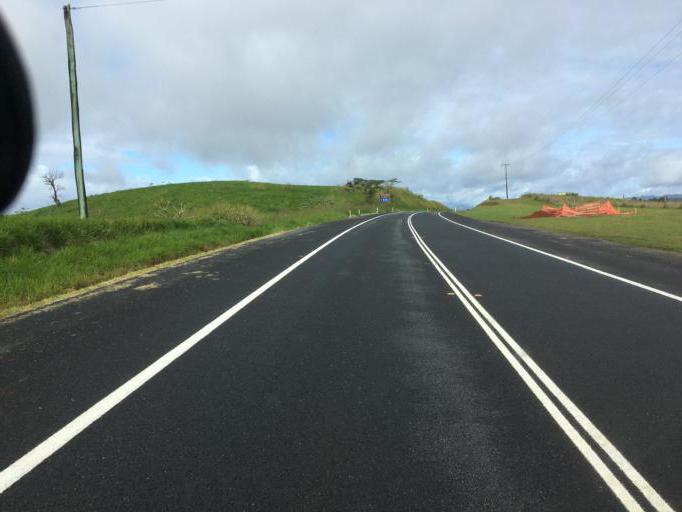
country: AU
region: Queensland
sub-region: Tablelands
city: Ravenshoe
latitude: -17.5360
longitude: 145.6638
